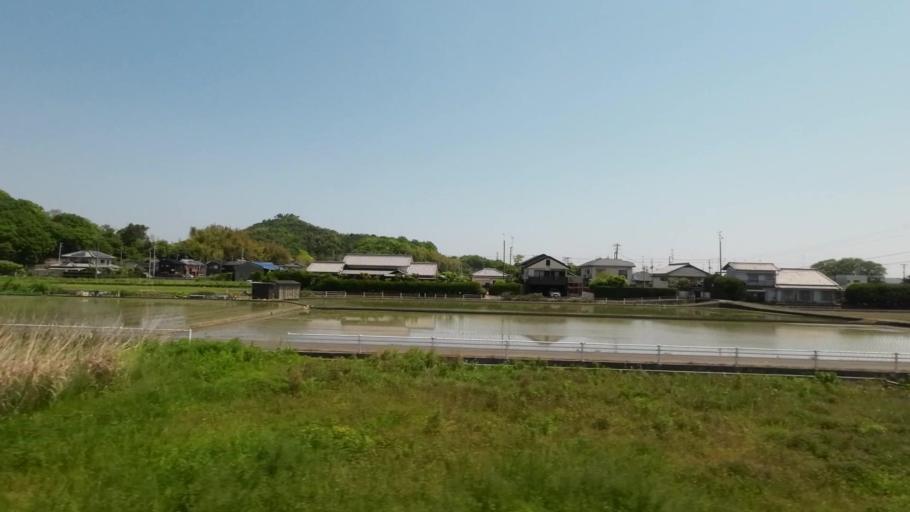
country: JP
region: Ehime
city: Saijo
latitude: 34.0201
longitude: 133.0282
